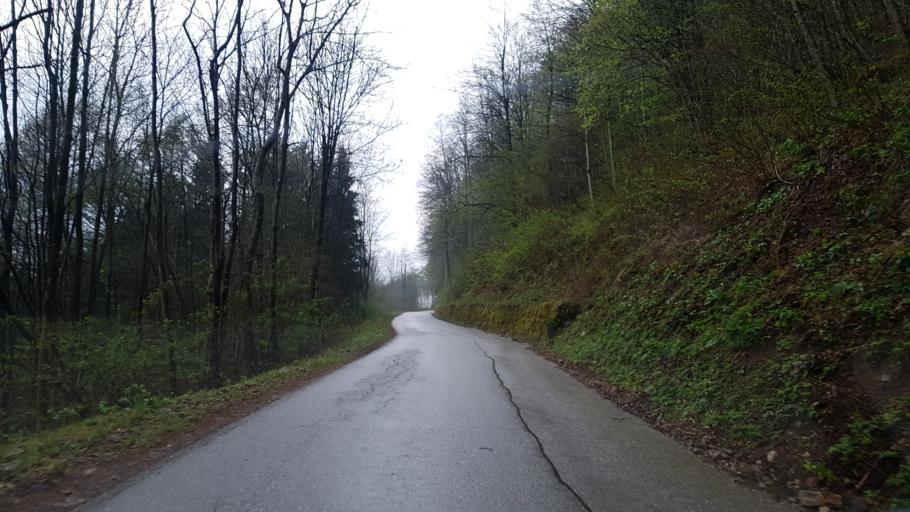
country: SI
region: Tolmin
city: Tolmin
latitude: 46.1262
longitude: 13.7872
